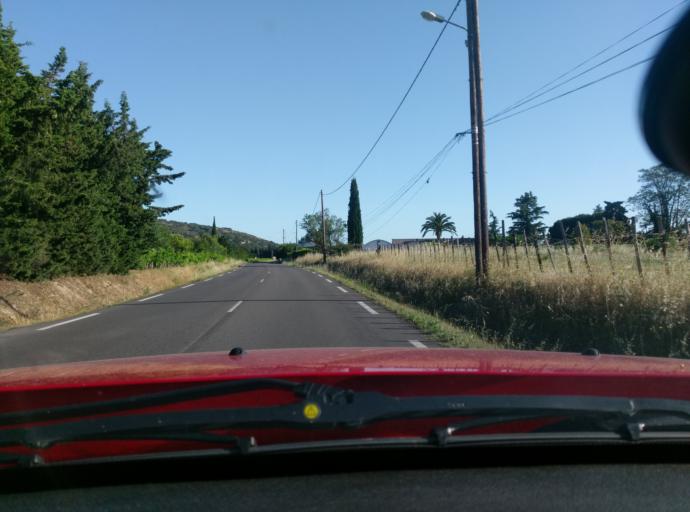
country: FR
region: Languedoc-Roussillon
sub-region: Departement du Gard
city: Sernhac
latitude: 43.9202
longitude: 4.5644
